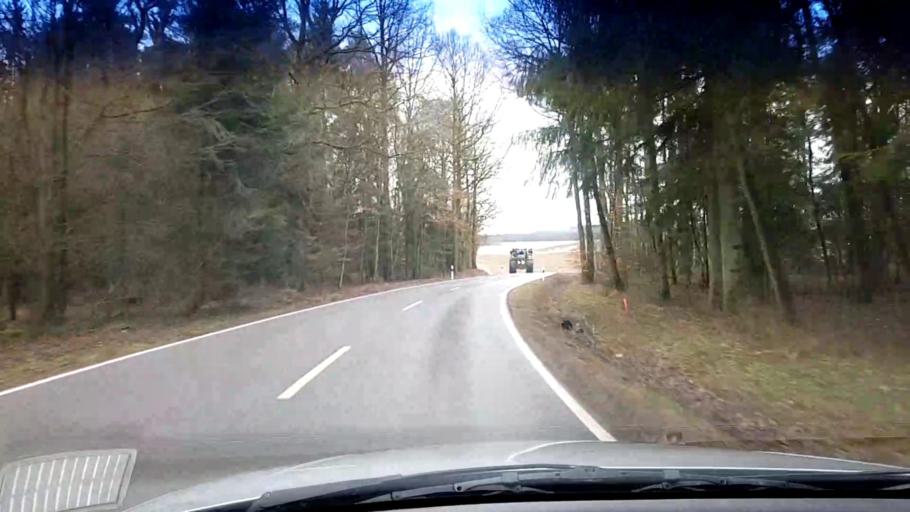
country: DE
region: Bavaria
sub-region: Upper Franconia
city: Zapfendorf
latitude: 50.0060
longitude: 10.9750
